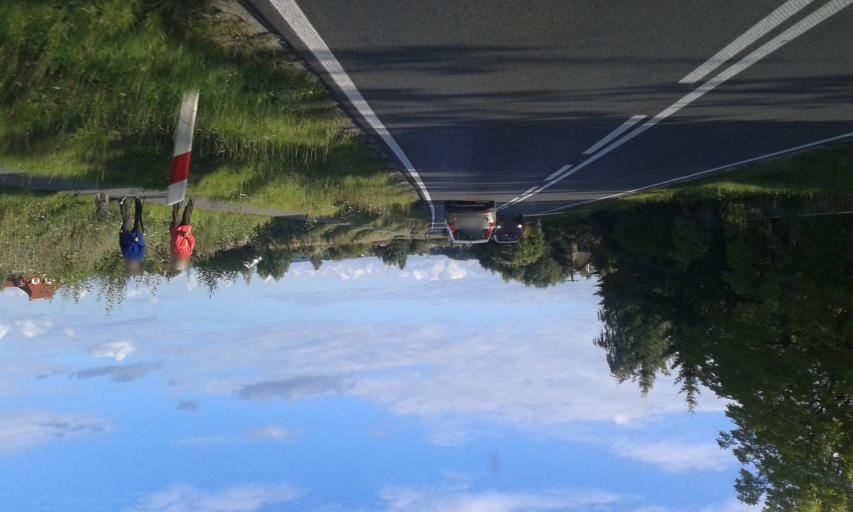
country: PL
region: West Pomeranian Voivodeship
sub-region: Koszalin
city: Koszalin
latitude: 54.1295
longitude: 16.1695
